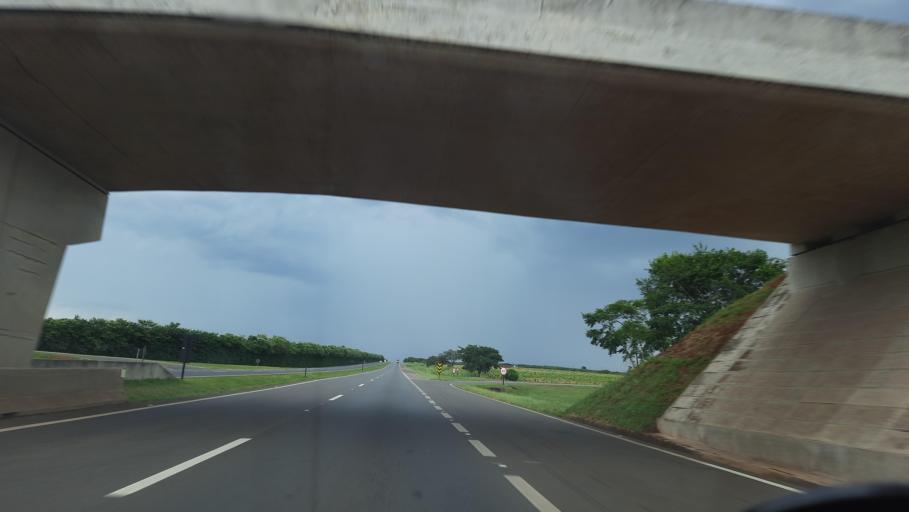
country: BR
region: Sao Paulo
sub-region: Aguai
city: Aguai
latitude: -22.0735
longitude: -47.0186
